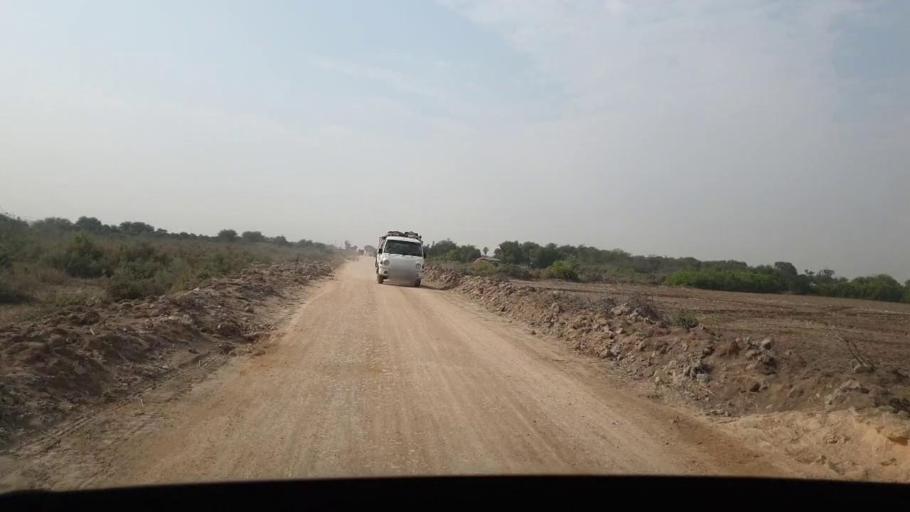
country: PK
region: Sindh
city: Chuhar Jamali
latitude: 24.3676
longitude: 67.9415
